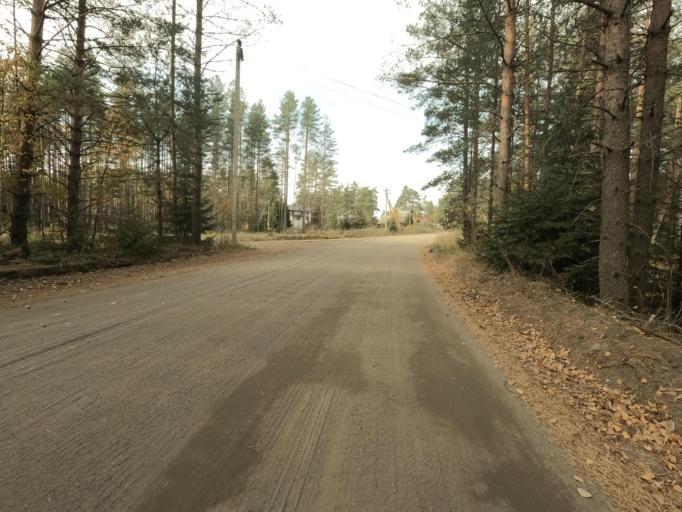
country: RU
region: Leningrad
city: Priladozhskiy
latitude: 59.6321
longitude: 31.3890
